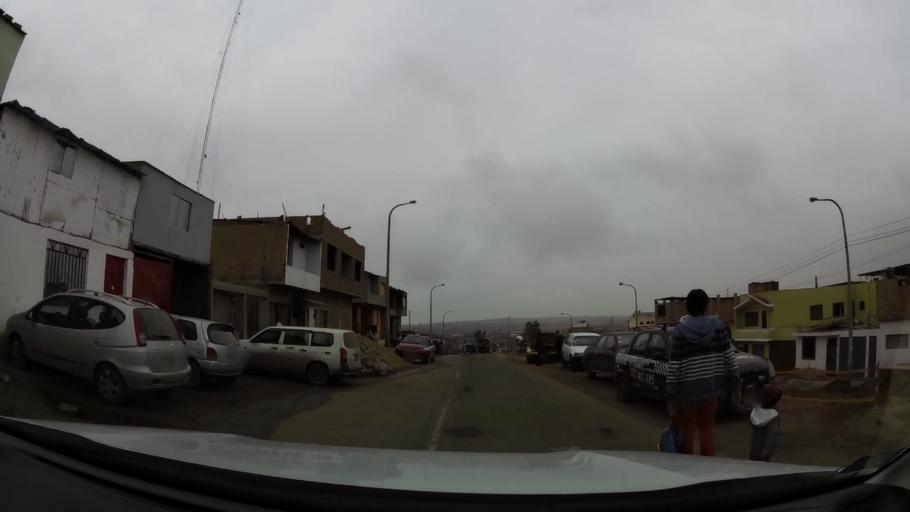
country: PE
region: Lima
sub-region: Lima
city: Punta Hermosa
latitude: -12.2372
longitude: -76.9081
